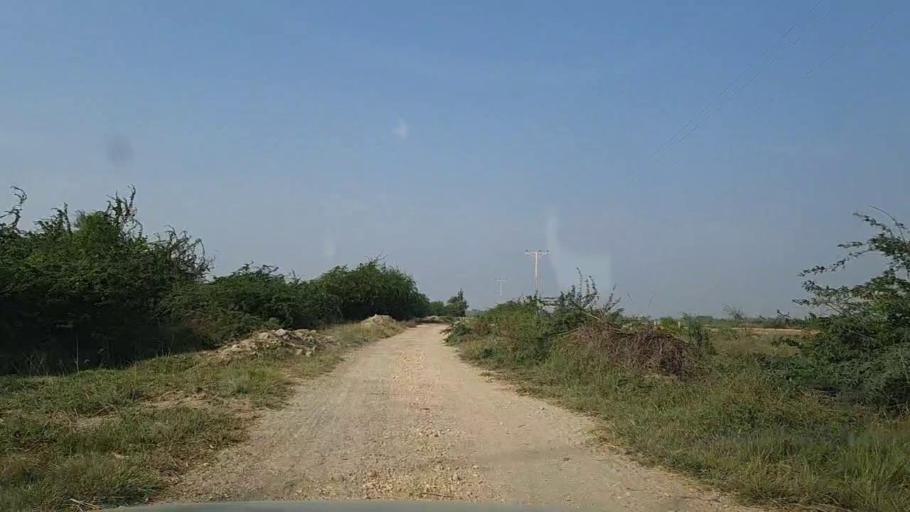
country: PK
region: Sindh
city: Mirpur Sakro
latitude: 24.5810
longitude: 67.5678
